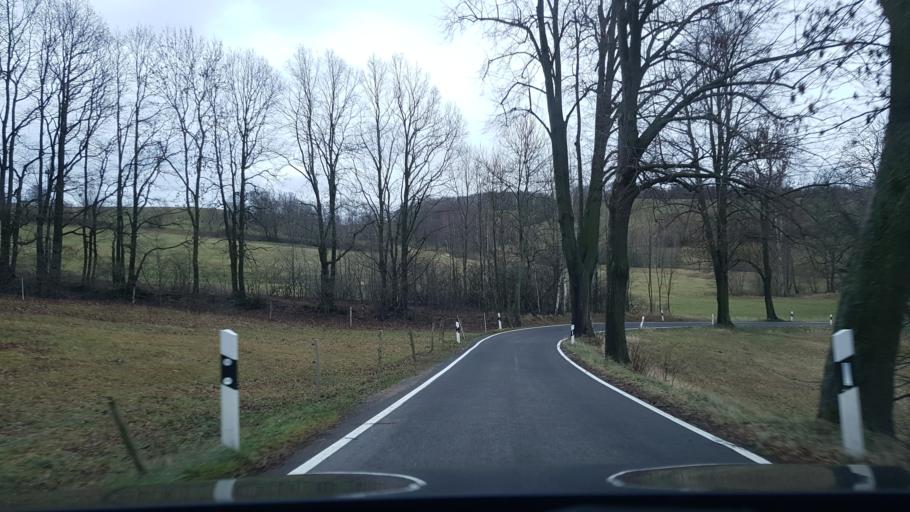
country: DE
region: Saxony
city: Liebstadt
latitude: 50.8350
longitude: 13.9096
